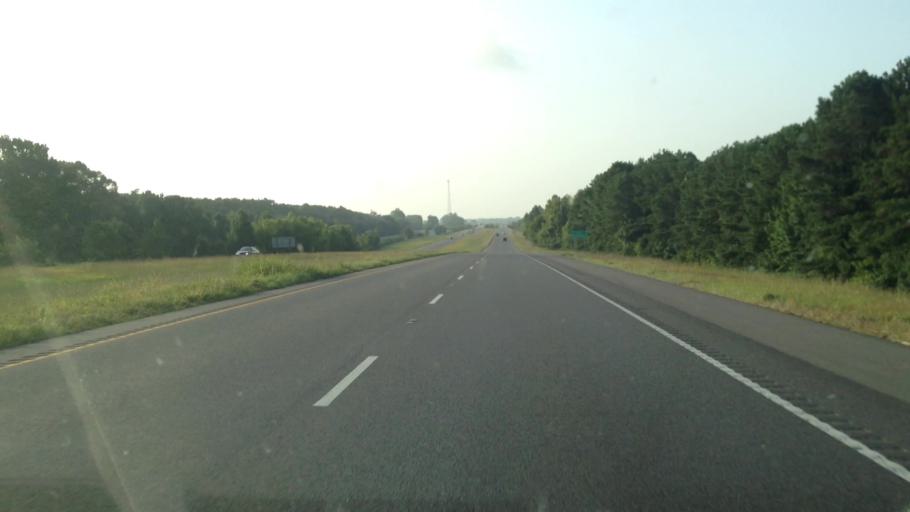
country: US
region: Louisiana
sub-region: Rapides Parish
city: Boyce
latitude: 31.4013
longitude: -92.7056
